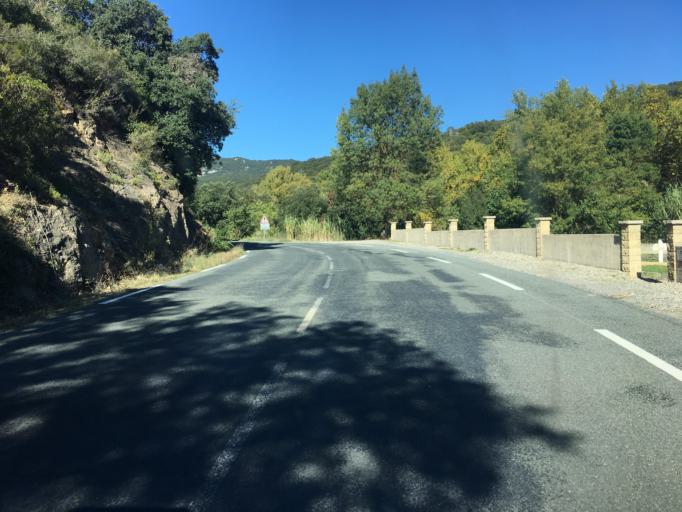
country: FR
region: Languedoc-Roussillon
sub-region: Departement de l'Herault
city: Nebian
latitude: 43.6100
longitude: 3.3831
